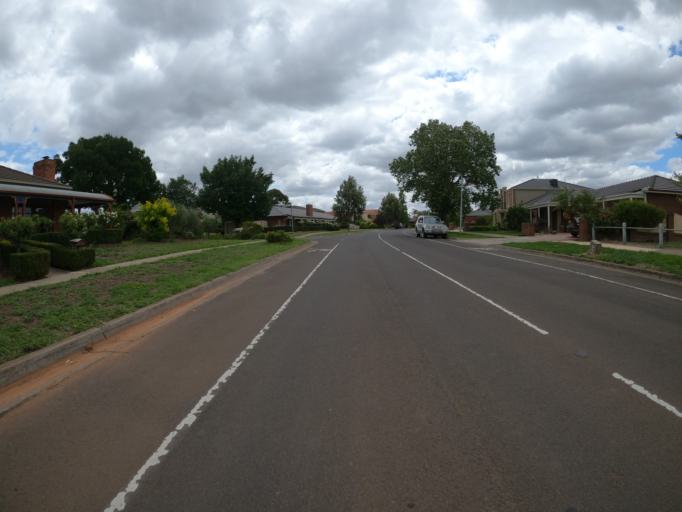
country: AU
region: Victoria
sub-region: Hume
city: Attwood
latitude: -37.6548
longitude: 144.8967
